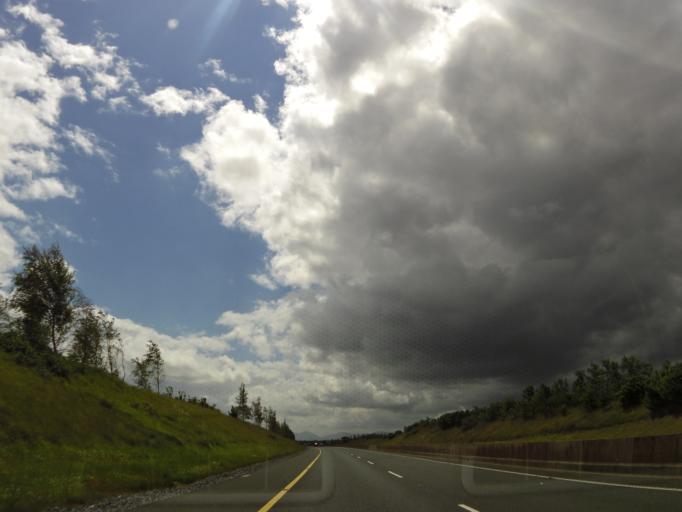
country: IE
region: Munster
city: Cashel
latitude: 52.4789
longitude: -7.9065
